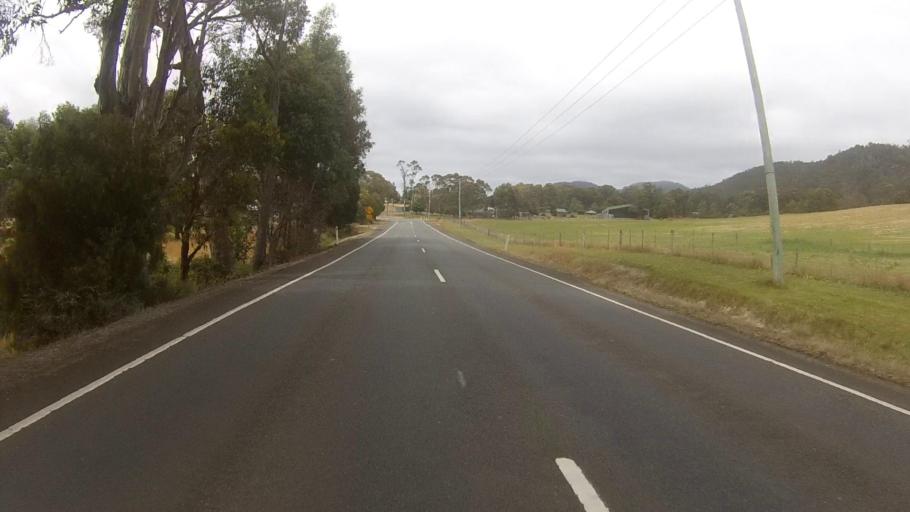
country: AU
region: Tasmania
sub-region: Kingborough
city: Margate
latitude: -42.9897
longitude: 147.1977
